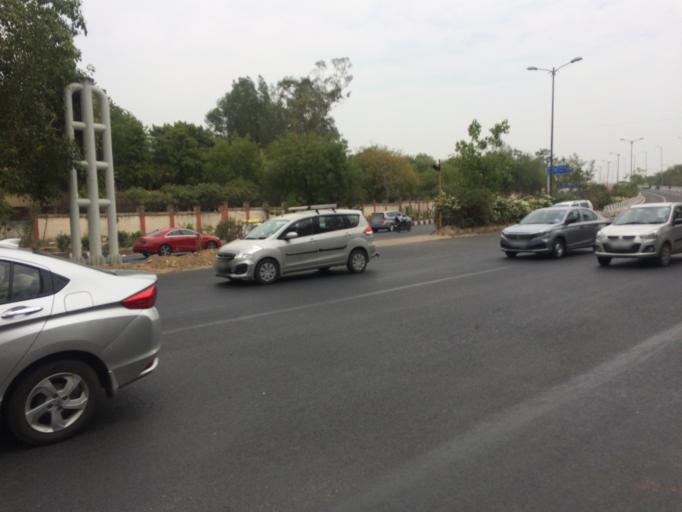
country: IN
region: NCT
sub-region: Central Delhi
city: Karol Bagh
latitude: 28.5740
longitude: 77.1521
